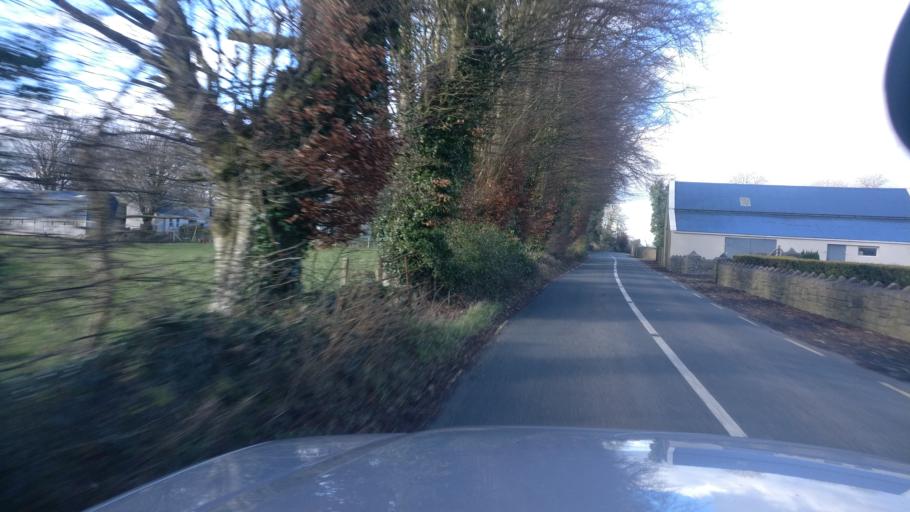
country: IE
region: Connaught
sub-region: County Galway
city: Loughrea
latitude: 53.1789
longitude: -8.3954
